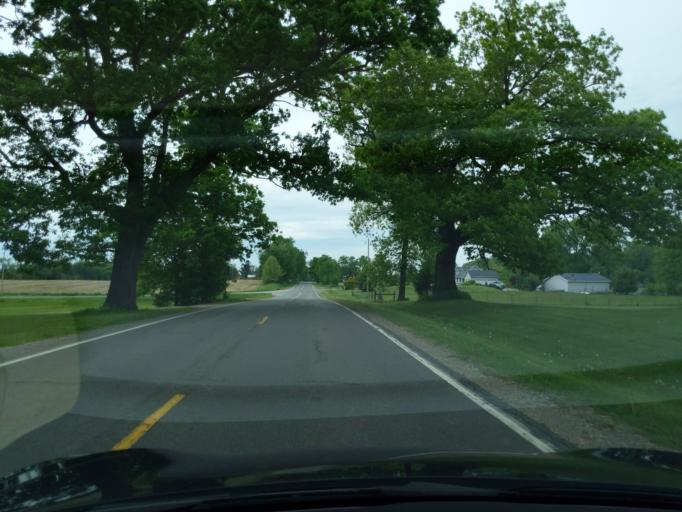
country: US
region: Michigan
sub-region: Ingham County
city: Leslie
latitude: 42.4471
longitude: -84.3560
